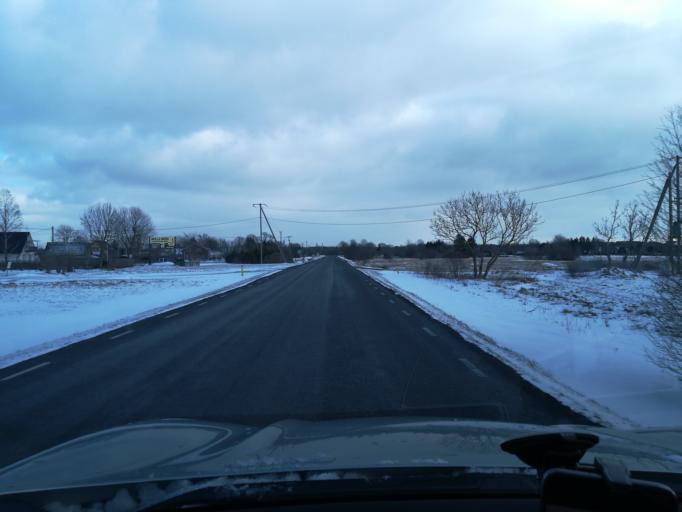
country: EE
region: Harju
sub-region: Harku vald
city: Tabasalu
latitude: 59.4284
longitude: 24.4126
